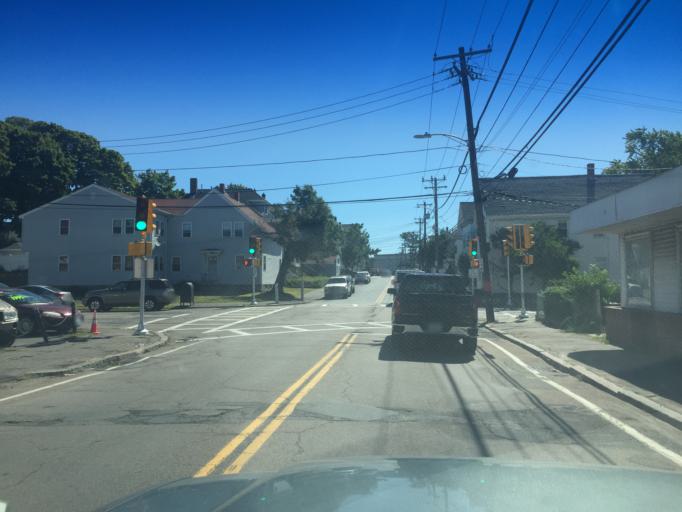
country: US
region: Massachusetts
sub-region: Norfolk County
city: Quincy
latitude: 42.2412
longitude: -71.0102
